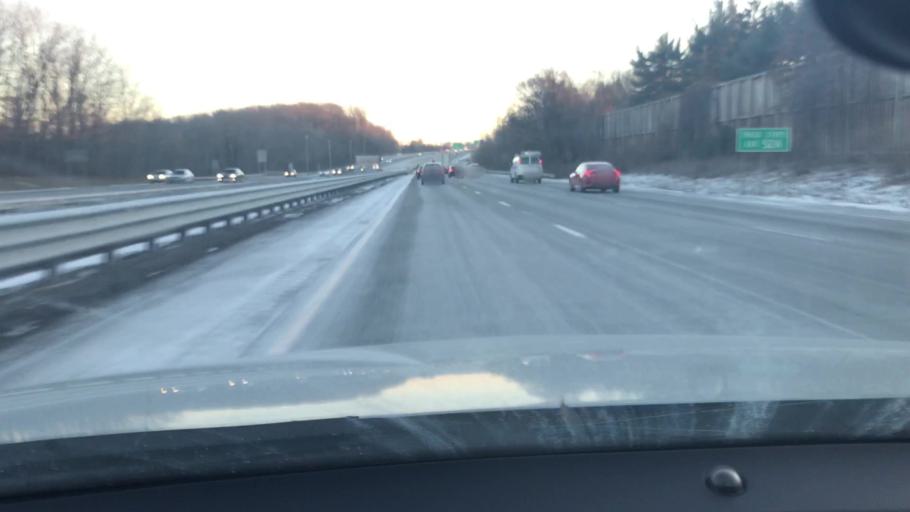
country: US
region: New Jersey
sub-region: Burlington County
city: Bordentown
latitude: 40.1435
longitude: -74.7184
